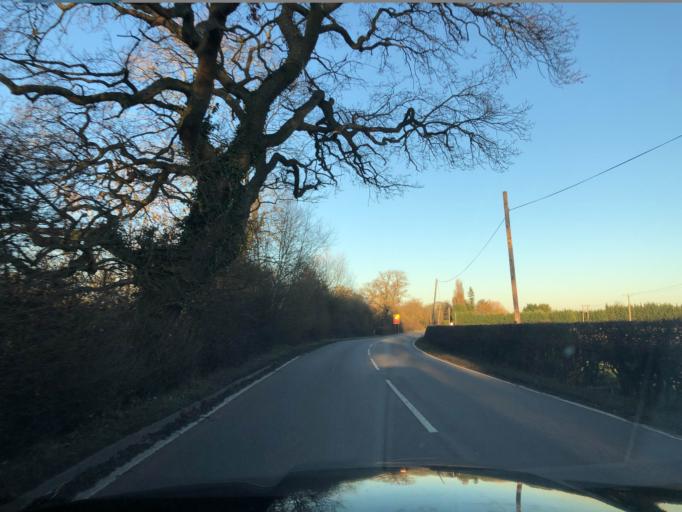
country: GB
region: England
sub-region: Warwickshire
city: Harbury
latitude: 52.2046
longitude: -1.4453
